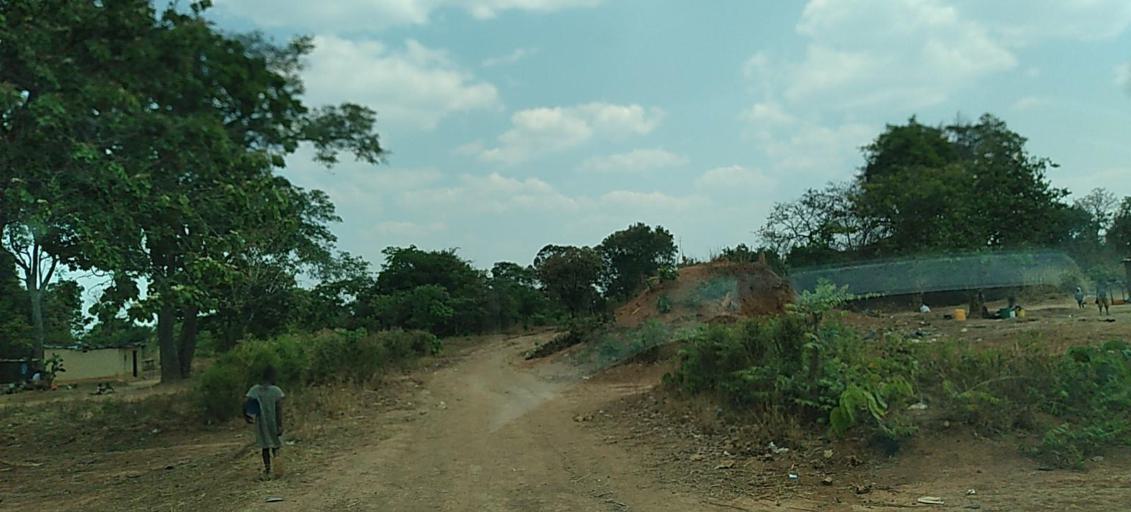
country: CD
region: Katanga
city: Kipushi
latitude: -12.0283
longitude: 27.4357
